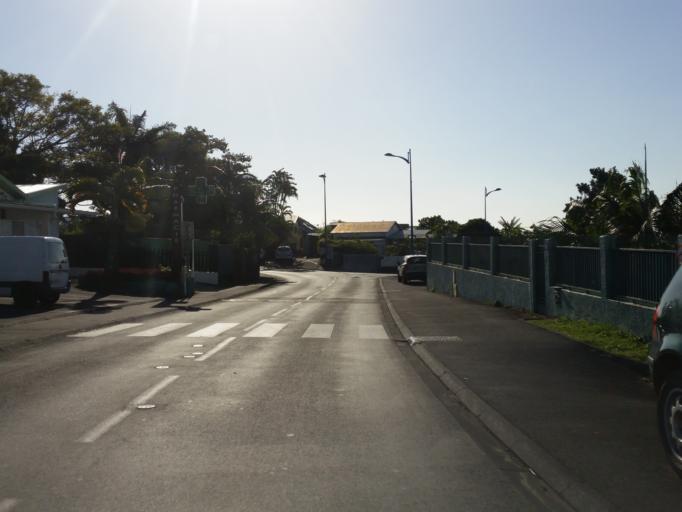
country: RE
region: Reunion
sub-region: Reunion
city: Sainte-Marie
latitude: -20.9256
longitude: 55.5216
